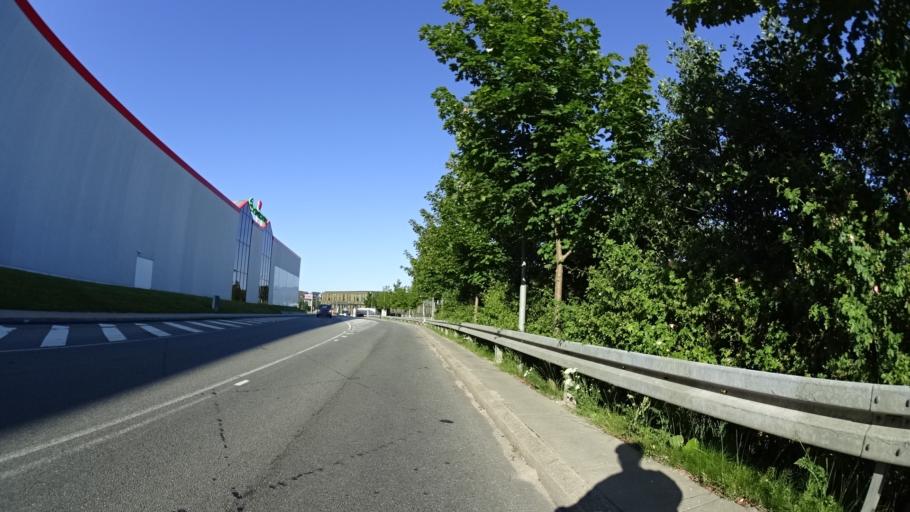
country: DK
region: Central Jutland
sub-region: Arhus Kommune
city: Stavtrup
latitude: 56.1182
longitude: 10.1529
